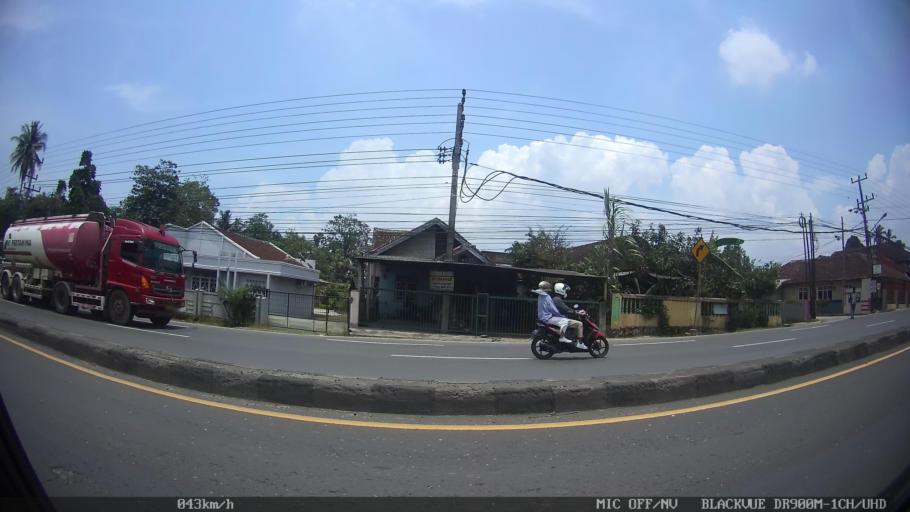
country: ID
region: Lampung
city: Kedaton
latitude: -5.3580
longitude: 105.2225
